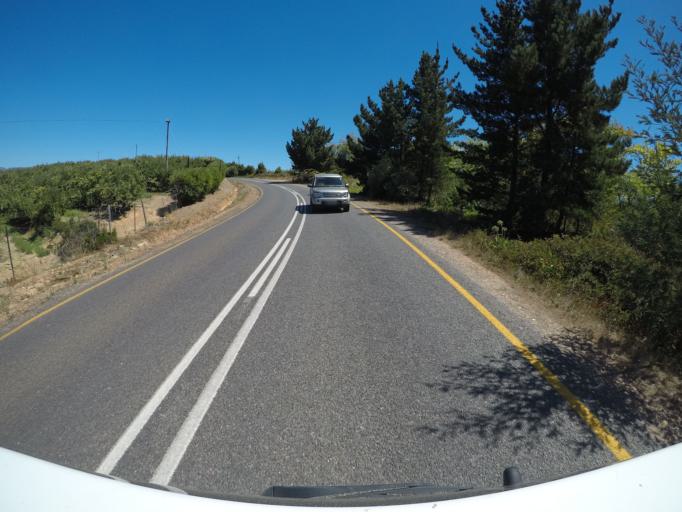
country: ZA
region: Western Cape
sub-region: Overberg District Municipality
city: Grabouw
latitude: -34.2109
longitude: 19.0516
